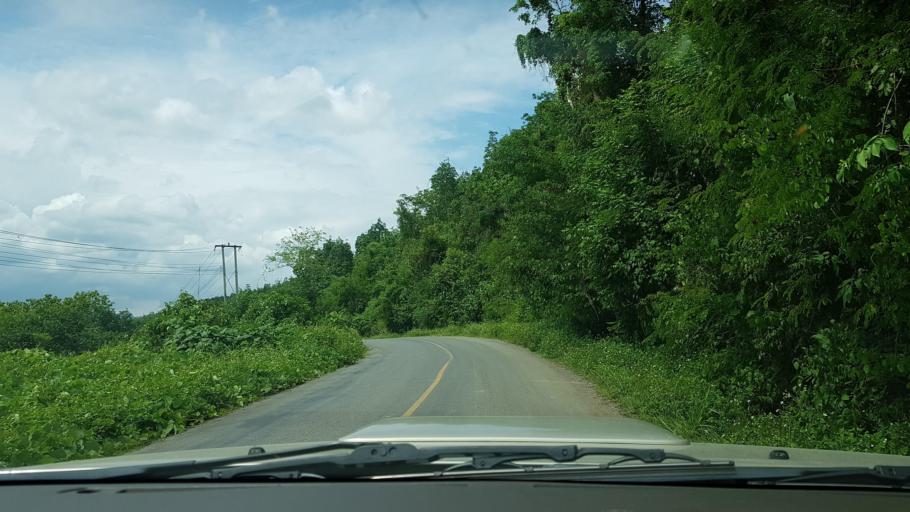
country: LA
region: Loungnamtha
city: Muang Nale
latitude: 20.2435
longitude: 101.5769
